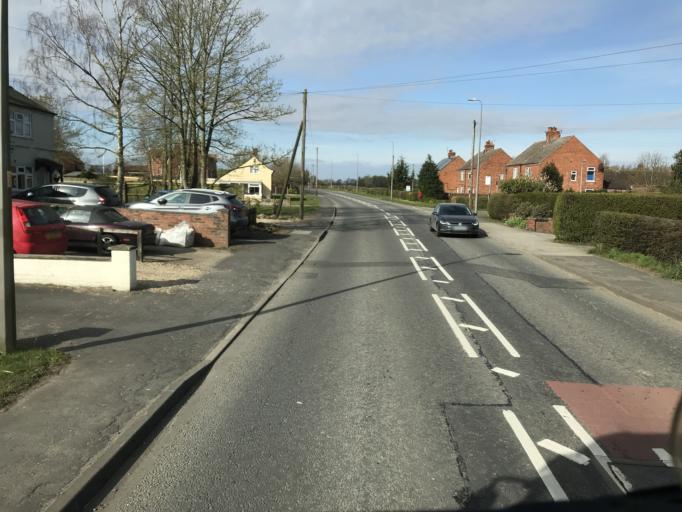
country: GB
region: England
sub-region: Lincolnshire
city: Market Rasen
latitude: 53.3864
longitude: -0.3696
